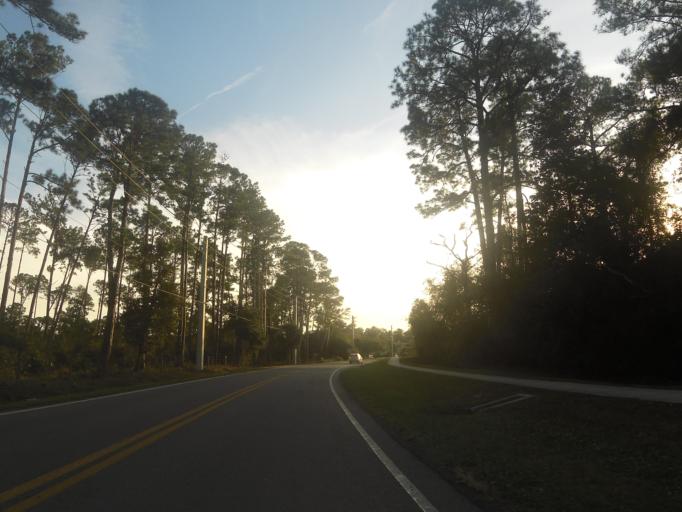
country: US
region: Florida
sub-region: Saint Johns County
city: Palm Valley
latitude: 30.1535
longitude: -81.3748
